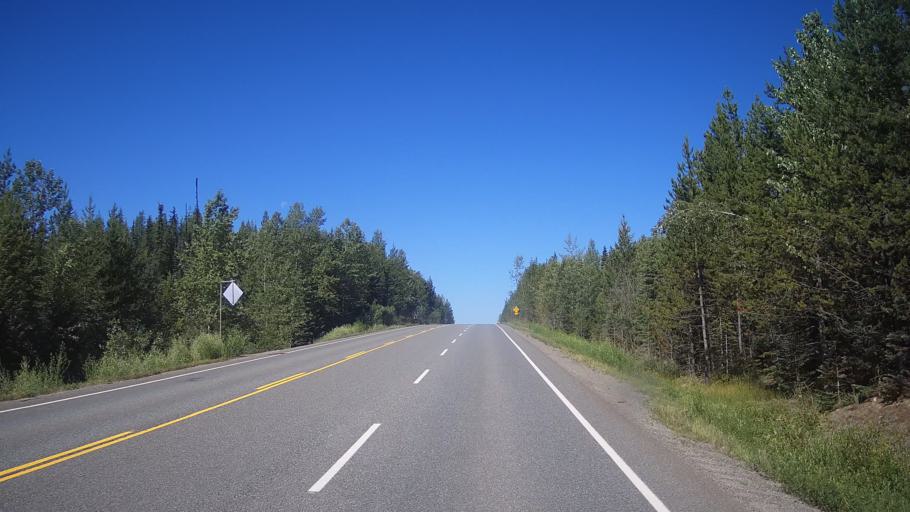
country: CA
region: British Columbia
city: Kamloops
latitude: 51.4976
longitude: -120.3724
